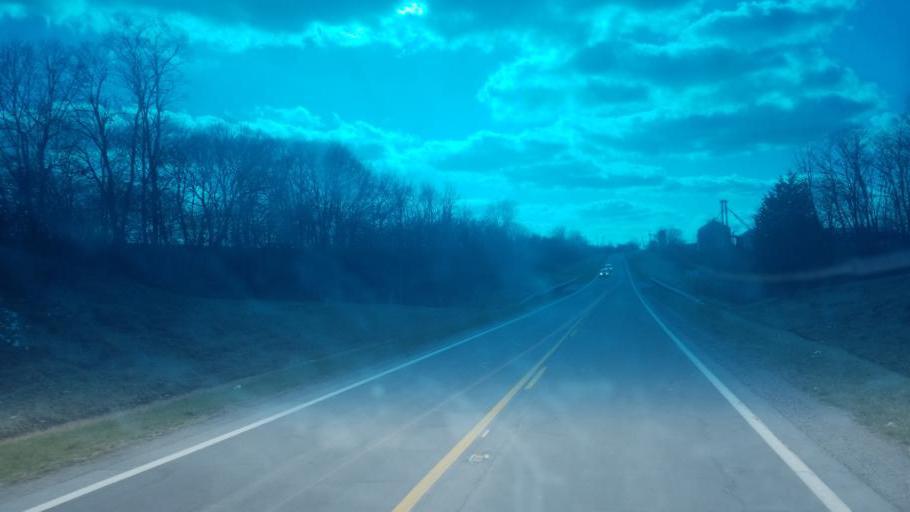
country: US
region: Ohio
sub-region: Highland County
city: Greenfield
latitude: 39.3461
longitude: -83.4127
